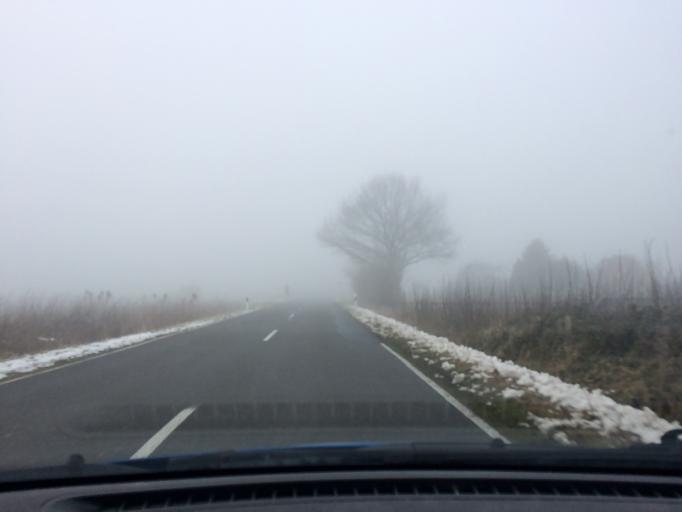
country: DE
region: Schleswig-Holstein
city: Krukow
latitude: 53.4217
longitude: 10.4894
